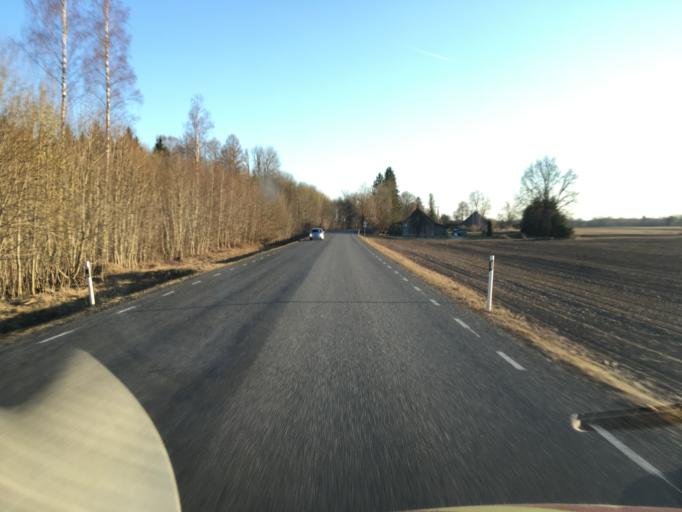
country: EE
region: Raplamaa
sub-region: Kehtna vald
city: Kehtna
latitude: 59.0451
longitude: 24.9446
